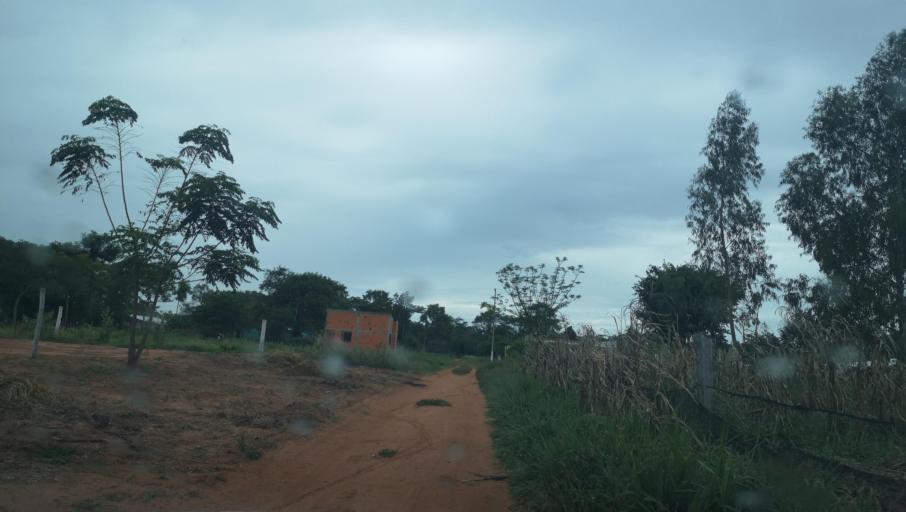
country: PY
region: San Pedro
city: Capiibary
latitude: -24.7204
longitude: -56.0115
